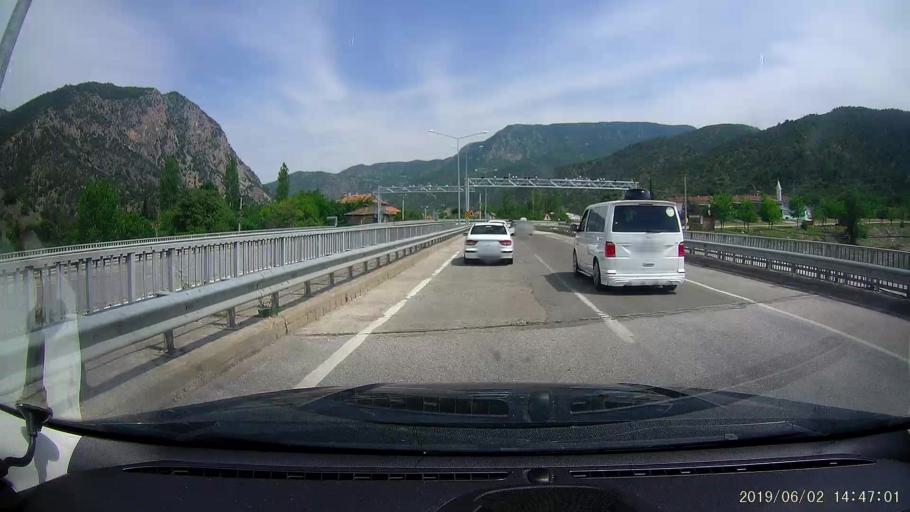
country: TR
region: Corum
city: Hacihamza
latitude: 41.0718
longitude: 34.4569
